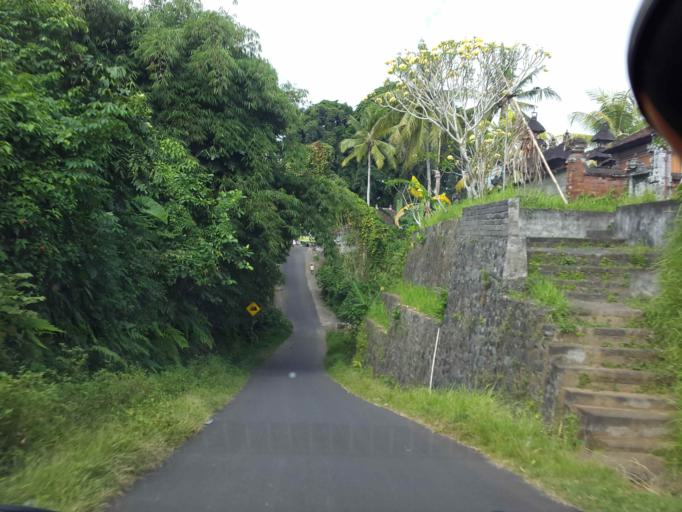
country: ID
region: Bali
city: Banjar Kelodan
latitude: -8.5182
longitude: 115.3740
